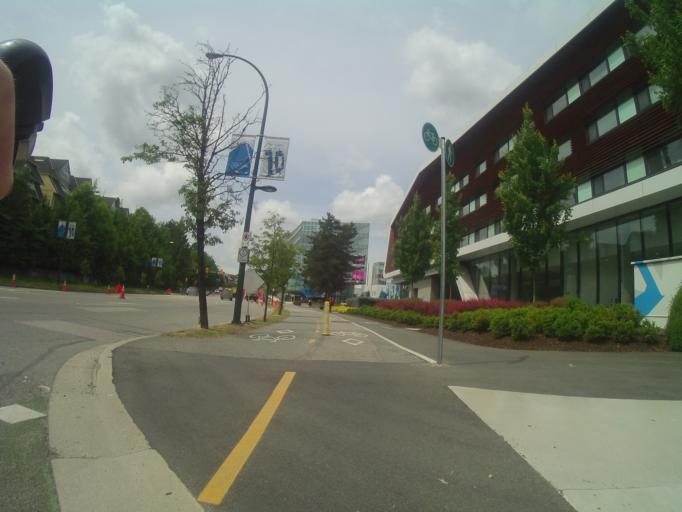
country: CA
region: British Columbia
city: Vancouver
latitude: 49.2668
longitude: -123.0892
